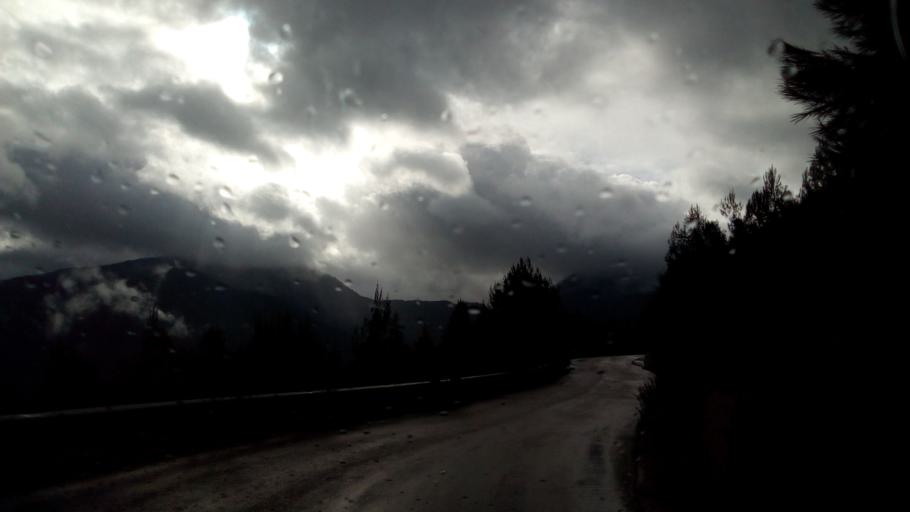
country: GR
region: West Greece
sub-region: Nomos Aitolias kai Akarnanias
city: Thermo
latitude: 38.6752
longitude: 21.8550
